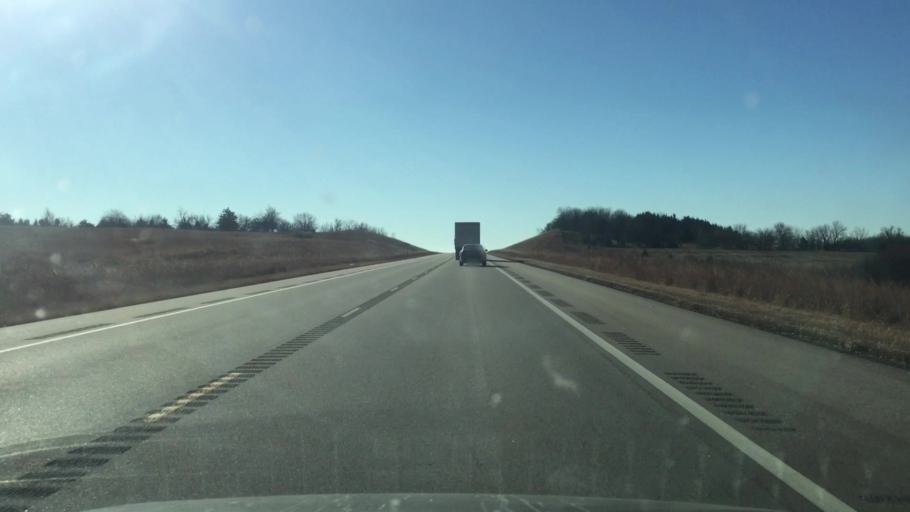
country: US
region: Kansas
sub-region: Allen County
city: Iola
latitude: 38.0158
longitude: -95.3807
